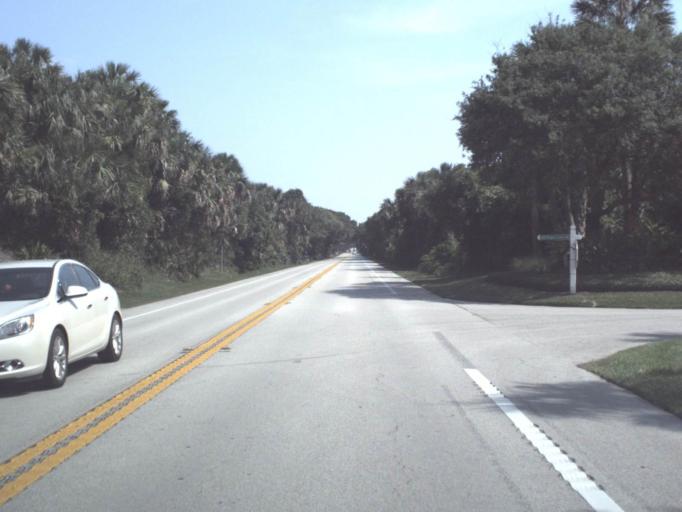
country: US
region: Florida
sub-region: Saint Johns County
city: Palm Valley
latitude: 30.1410
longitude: -81.3520
